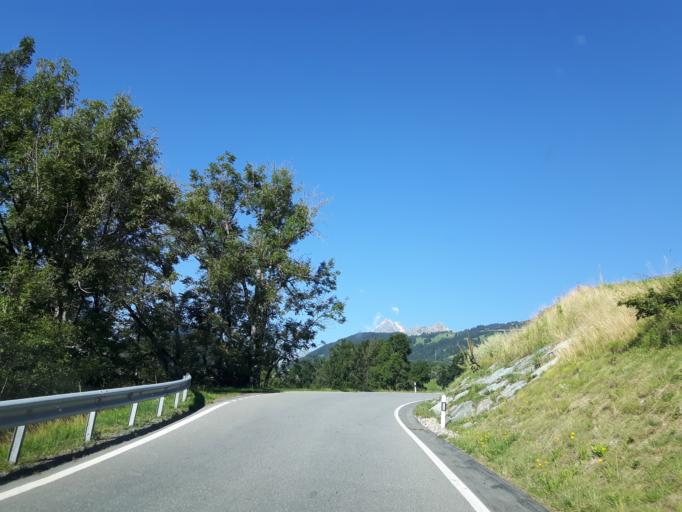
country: CH
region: Grisons
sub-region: Surselva District
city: Breil
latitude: 46.7771
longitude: 9.1288
